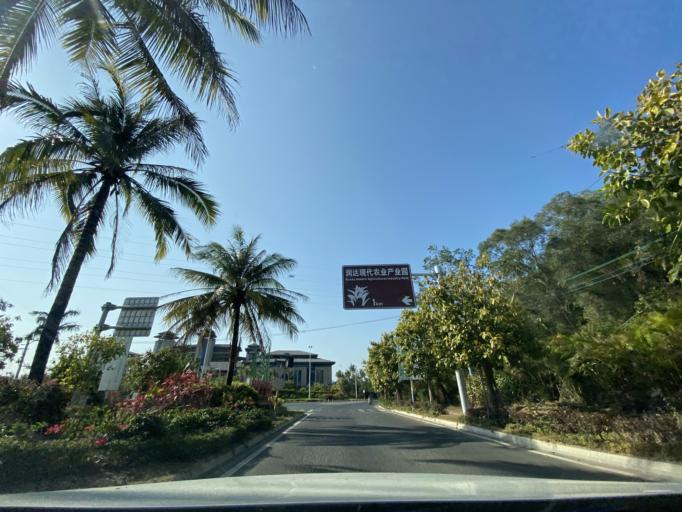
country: CN
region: Hainan
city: Yingzhou
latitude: 18.4438
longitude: 109.8466
